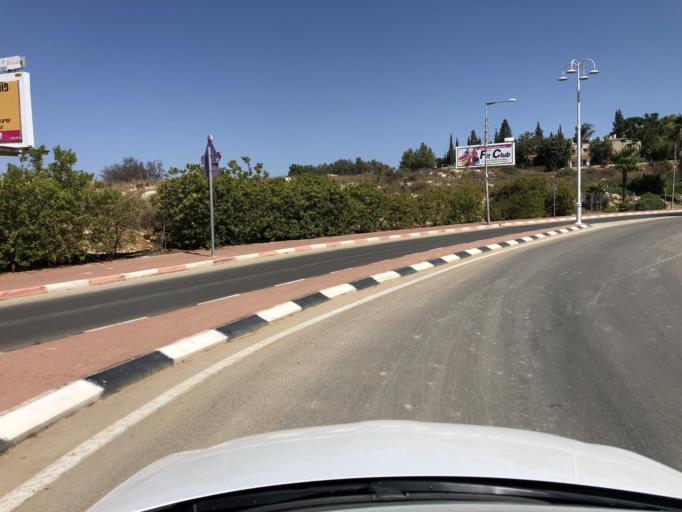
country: PS
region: West Bank
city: An Nabi Ilyas
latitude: 32.1720
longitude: 35.0035
